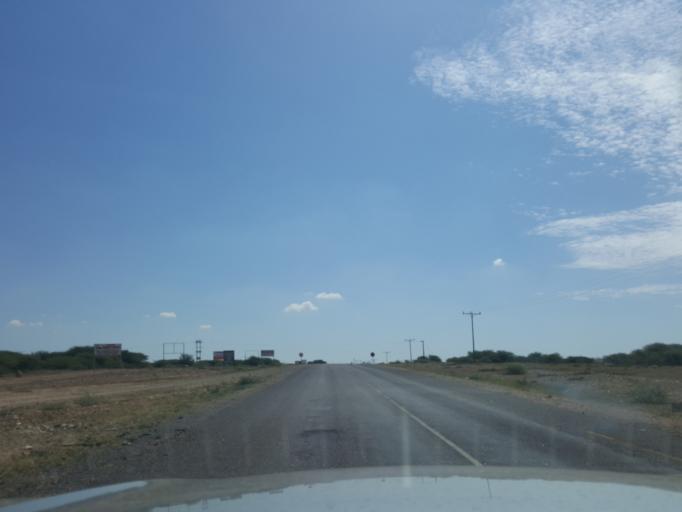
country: BW
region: Kweneng
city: Letlhakeng
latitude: -24.1177
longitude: 25.0500
